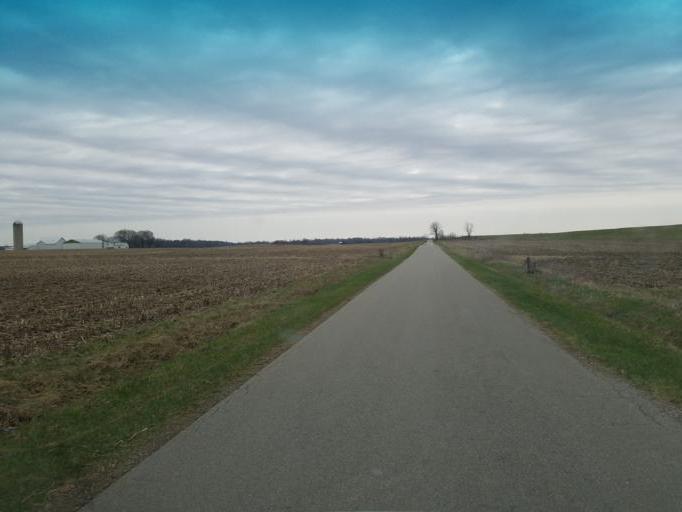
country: US
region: Ohio
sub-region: Crawford County
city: Bucyrus
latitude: 40.8460
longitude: -82.9307
